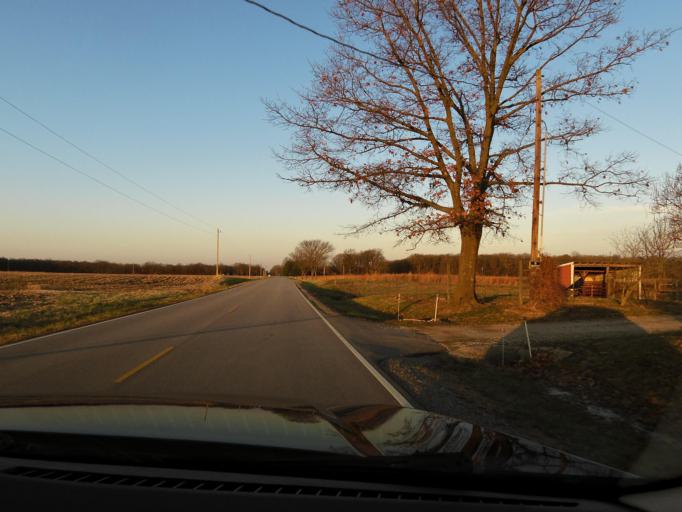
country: US
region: Illinois
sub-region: Marion County
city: Salem
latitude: 38.7588
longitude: -88.9173
